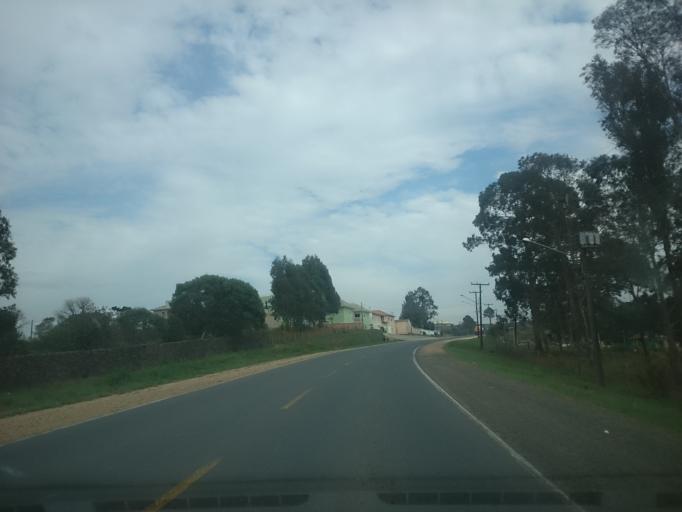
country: BR
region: Santa Catarina
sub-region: Lages
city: Lages
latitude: -27.7810
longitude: -50.3141
